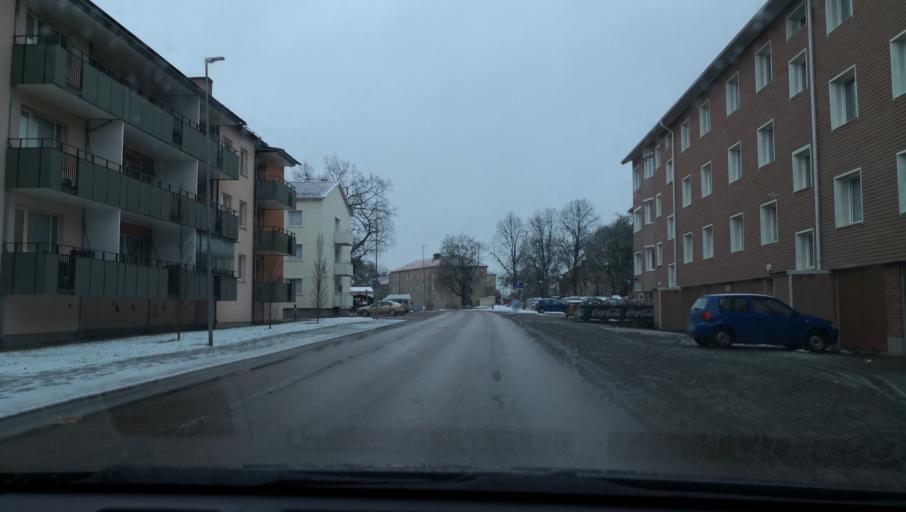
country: SE
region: Vaestmanland
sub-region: Kopings Kommun
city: Koping
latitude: 59.5224
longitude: 15.9895
